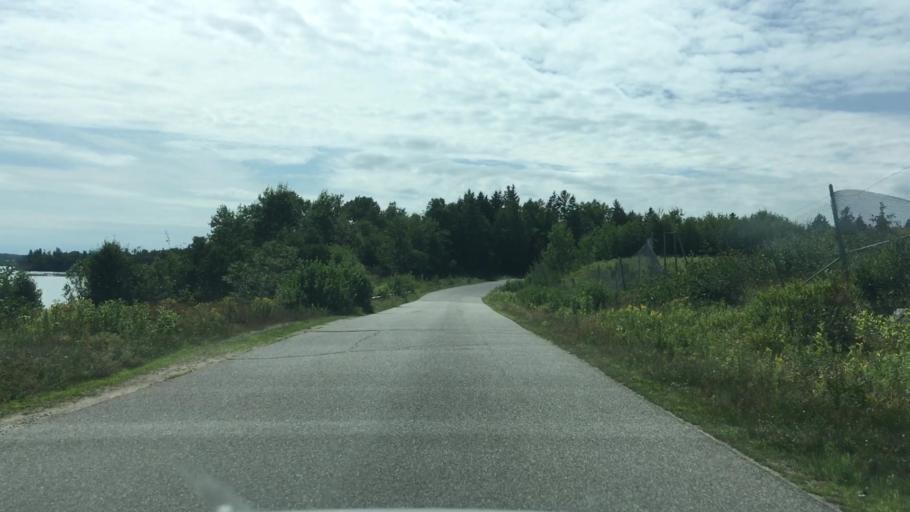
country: US
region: Maine
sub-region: Washington County
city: Eastport
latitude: 44.9063
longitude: -67.0048
